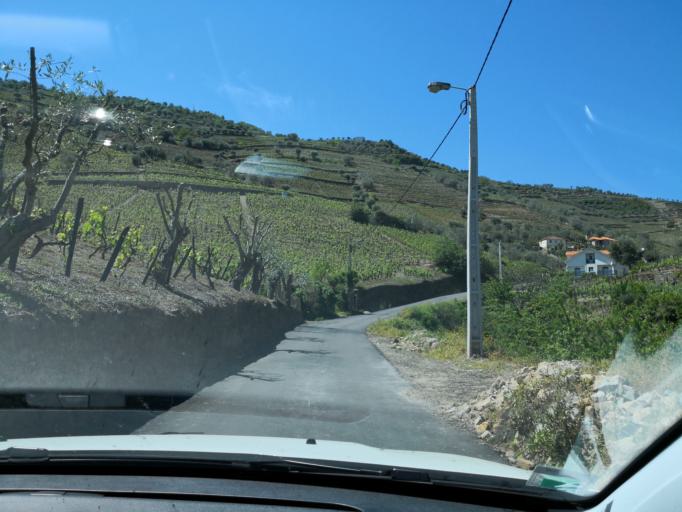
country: PT
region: Vila Real
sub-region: Vila Real
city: Vila Real
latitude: 41.2279
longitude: -7.7217
